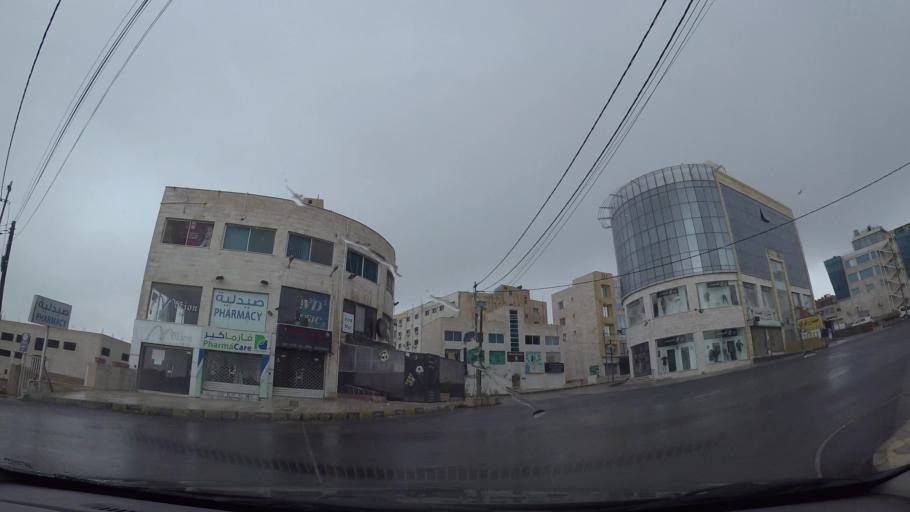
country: JO
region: Amman
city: Wadi as Sir
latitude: 31.9747
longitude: 35.8486
